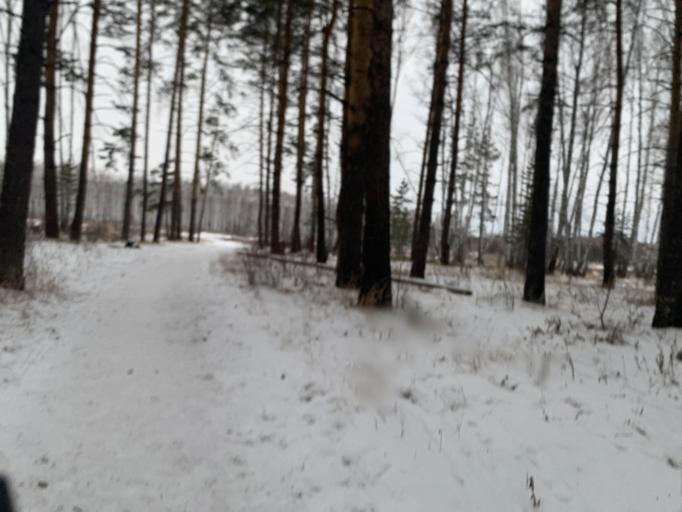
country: RU
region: Chelyabinsk
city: Roshchino
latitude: 55.2029
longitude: 61.2652
